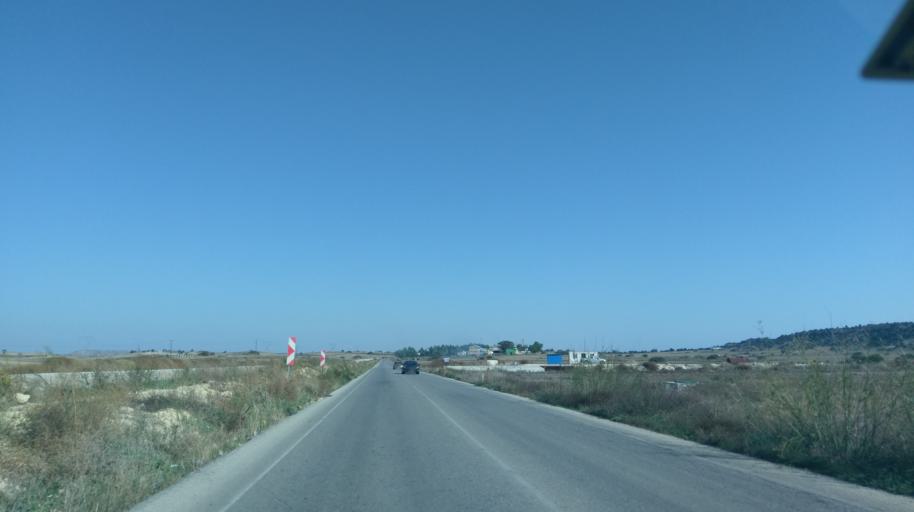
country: CY
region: Ammochostos
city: Trikomo
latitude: 35.3559
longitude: 34.0080
